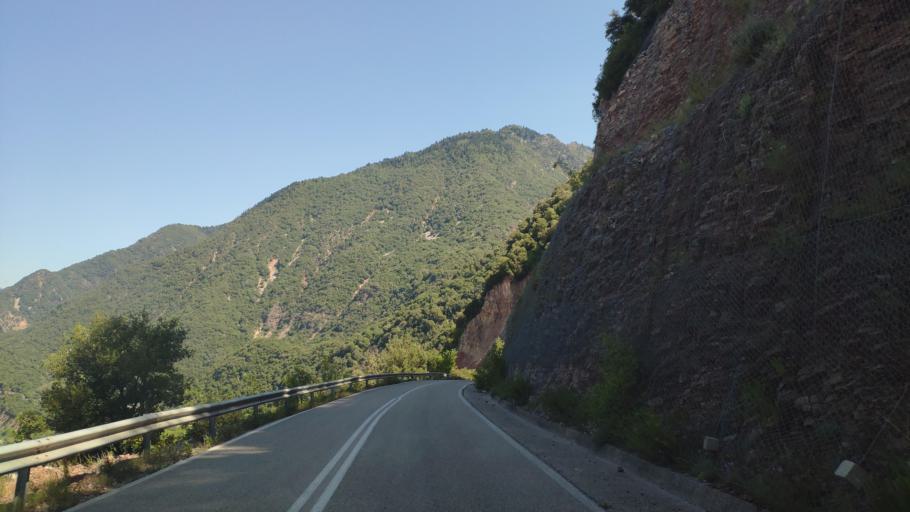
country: GR
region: Central Greece
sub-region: Nomos Evrytanias
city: Kerasochori
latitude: 39.0157
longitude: 21.5975
